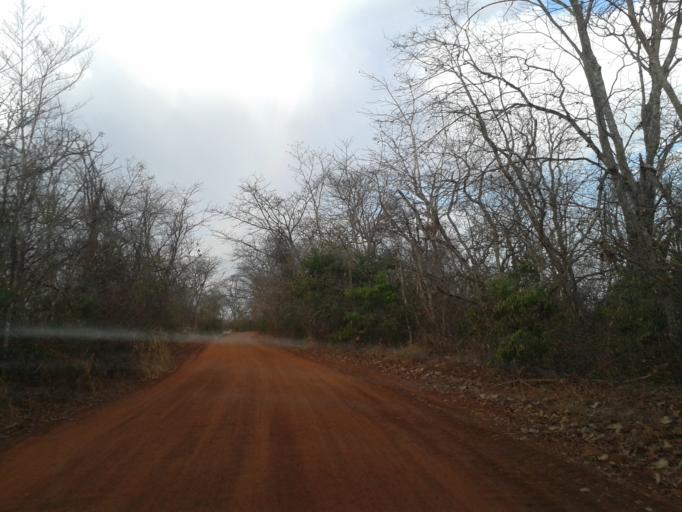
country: BR
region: Minas Gerais
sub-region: Santa Vitoria
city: Santa Vitoria
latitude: -19.1853
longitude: -49.8614
